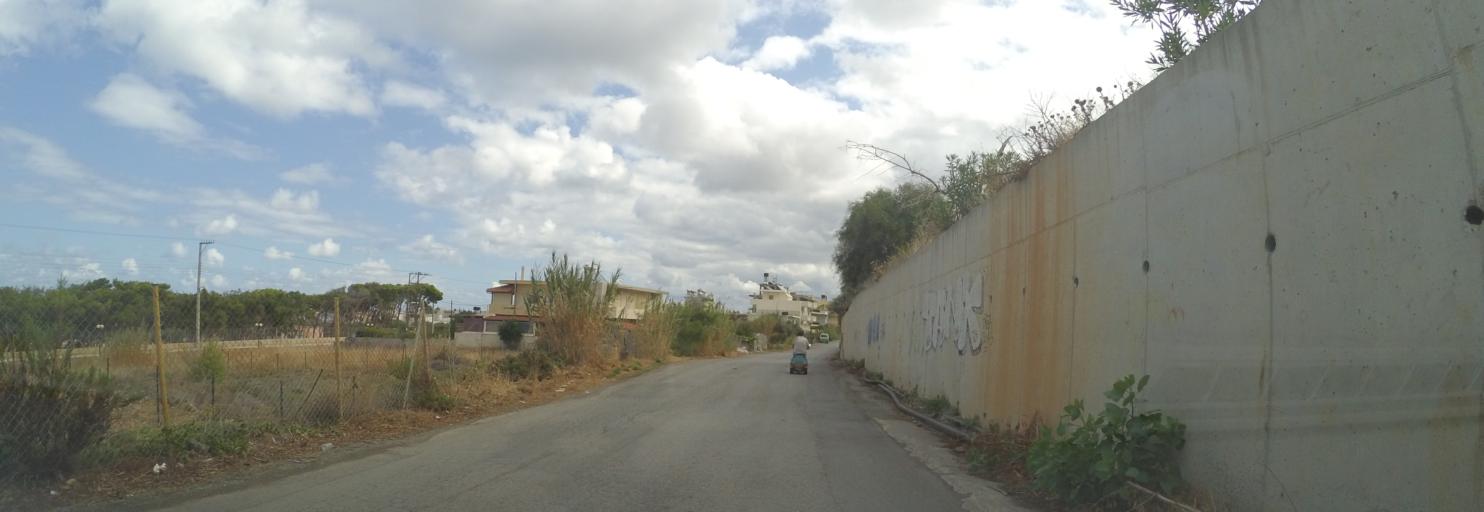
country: GR
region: Crete
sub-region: Nomos Irakleiou
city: Kokkini Hani
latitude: 35.3292
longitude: 25.2662
